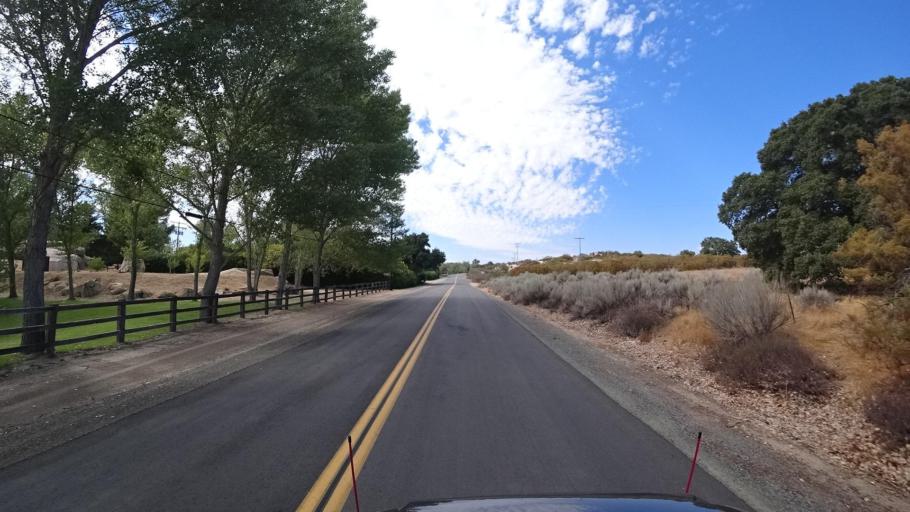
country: MX
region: Baja California
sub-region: Tecate
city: Cereso del Hongo
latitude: 32.6463
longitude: -116.2871
